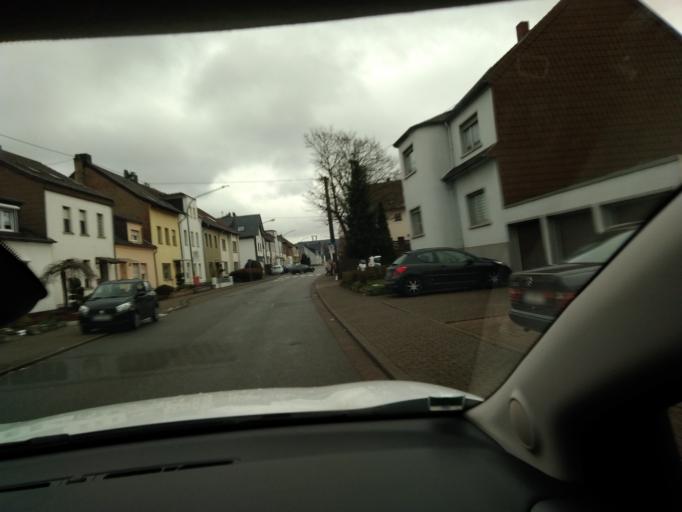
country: DE
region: Saarland
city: Saarlouis
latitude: 49.3309
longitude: 6.7573
